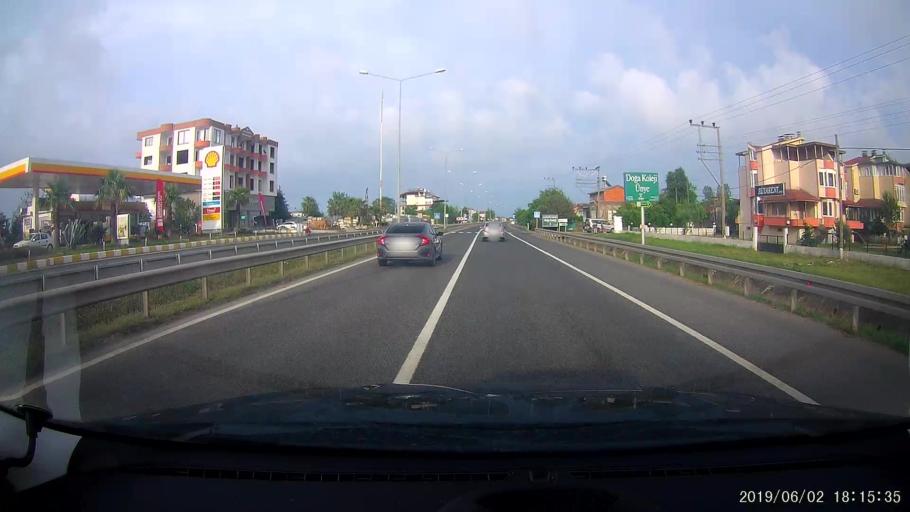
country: TR
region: Ordu
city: Unieh
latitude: 41.1057
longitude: 37.3812
